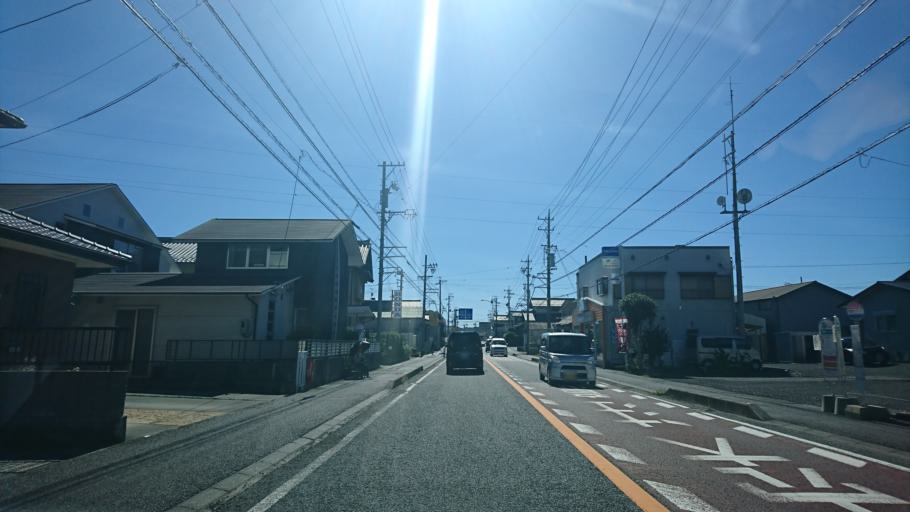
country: JP
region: Shizuoka
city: Shimada
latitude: 34.8405
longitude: 138.1802
